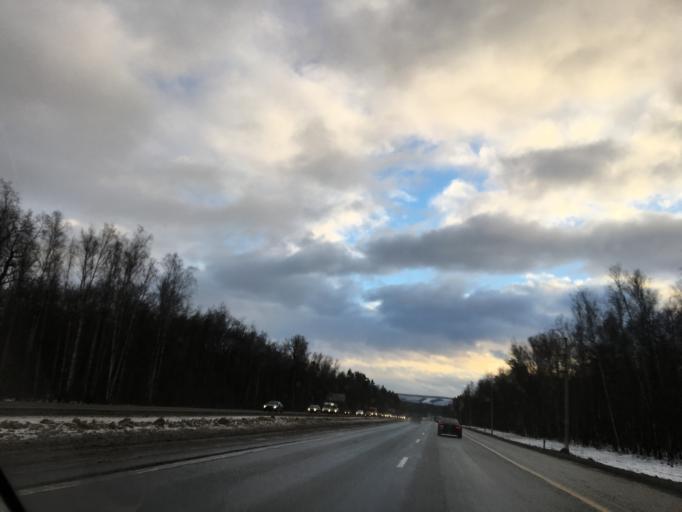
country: RU
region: Moskovskaya
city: Danki
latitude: 54.8976
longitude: 37.5116
